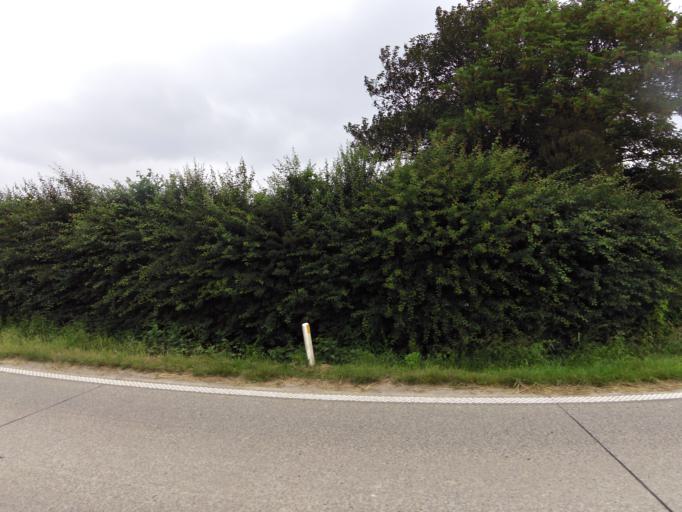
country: FR
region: Nord-Pas-de-Calais
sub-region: Departement du Nord
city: Saint-Jans-Cappel
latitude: 50.7741
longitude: 2.7759
